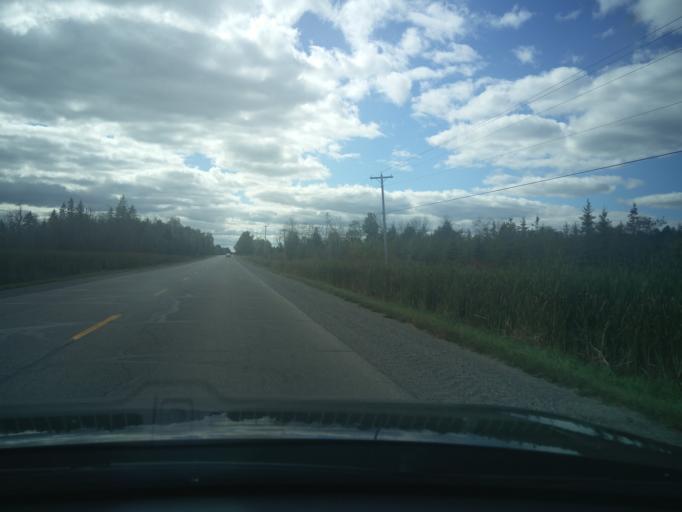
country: CA
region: Ontario
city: Carleton Place
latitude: 45.0661
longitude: -76.0334
